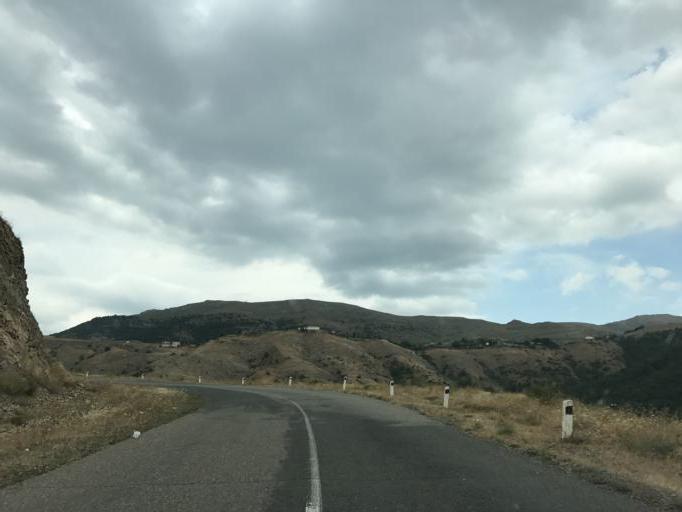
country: AZ
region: Lacin
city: Lacin
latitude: 39.6822
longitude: 46.6405
